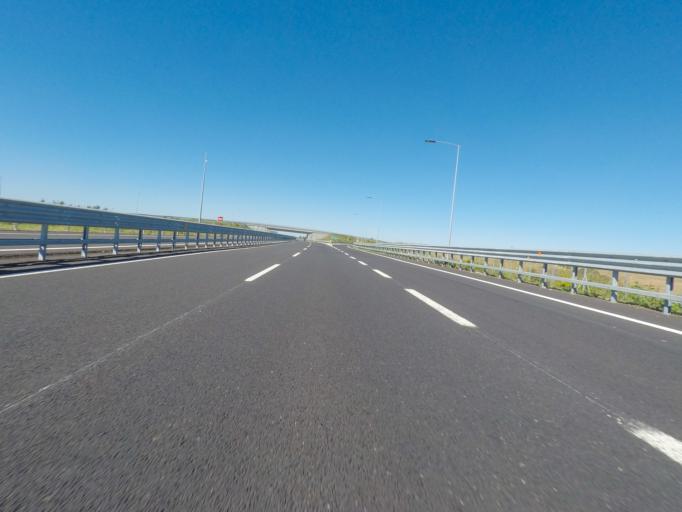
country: IT
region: Latium
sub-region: Provincia di Viterbo
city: Tarquinia
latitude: 42.2099
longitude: 11.7820
